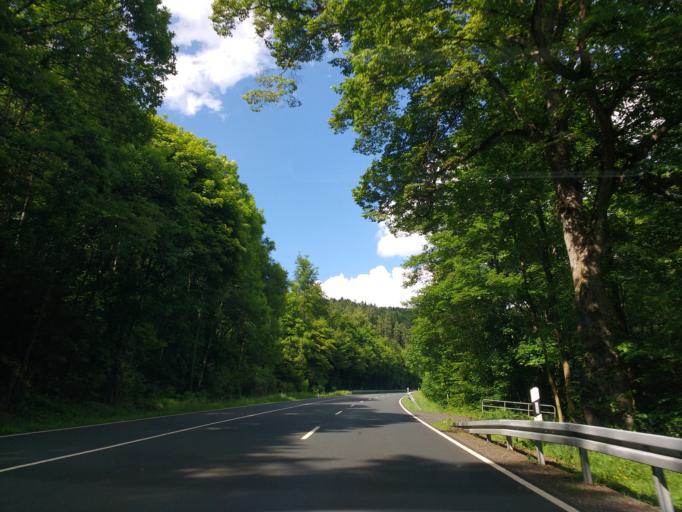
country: DE
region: Hesse
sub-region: Regierungsbezirk Giessen
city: Biedenkopf
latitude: 50.9374
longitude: 8.5370
